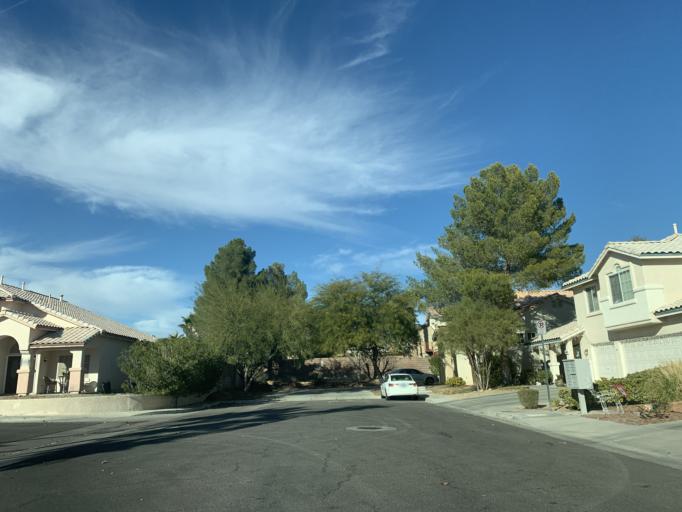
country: US
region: Nevada
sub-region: Clark County
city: Summerlin South
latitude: 36.1272
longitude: -115.3067
